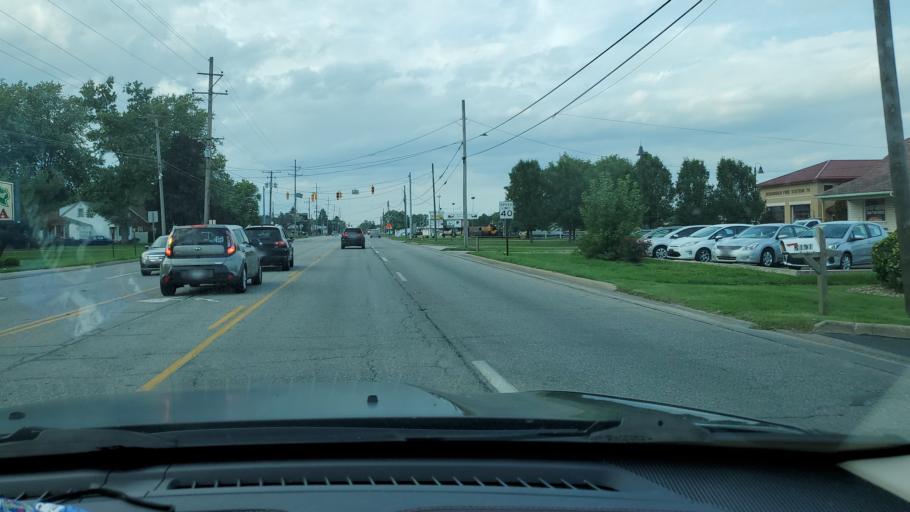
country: US
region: Ohio
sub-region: Mahoning County
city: Poland
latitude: 41.0356
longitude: -80.6346
